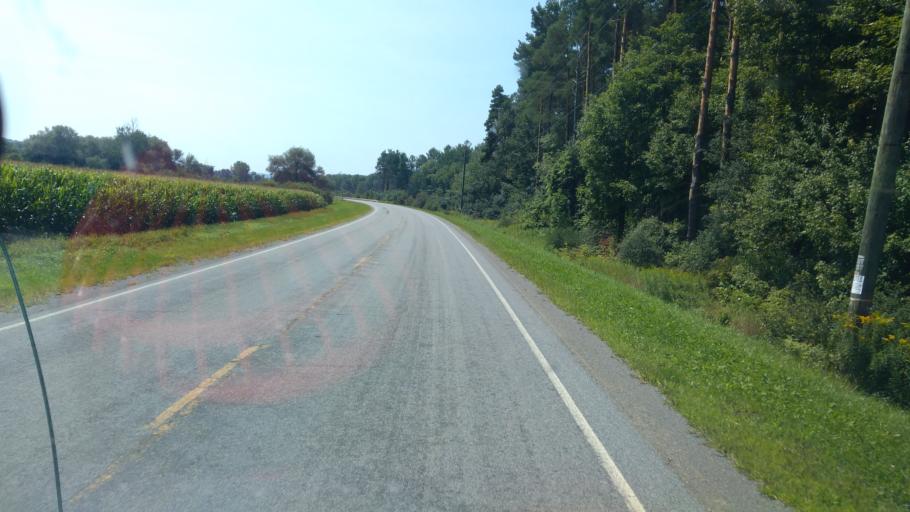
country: US
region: New York
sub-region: Allegany County
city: Alfred
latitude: 42.3504
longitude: -77.9237
